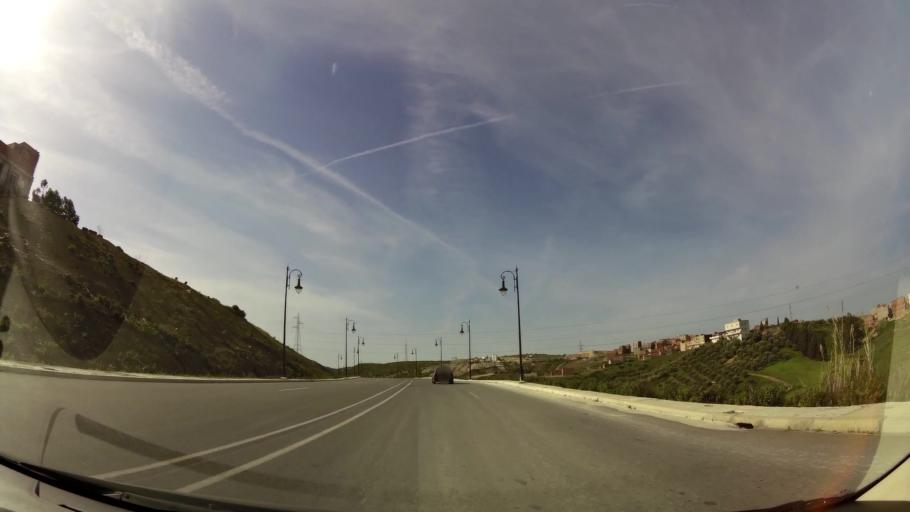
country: MA
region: Tanger-Tetouan
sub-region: Tanger-Assilah
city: Tangier
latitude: 35.7225
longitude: -5.7667
